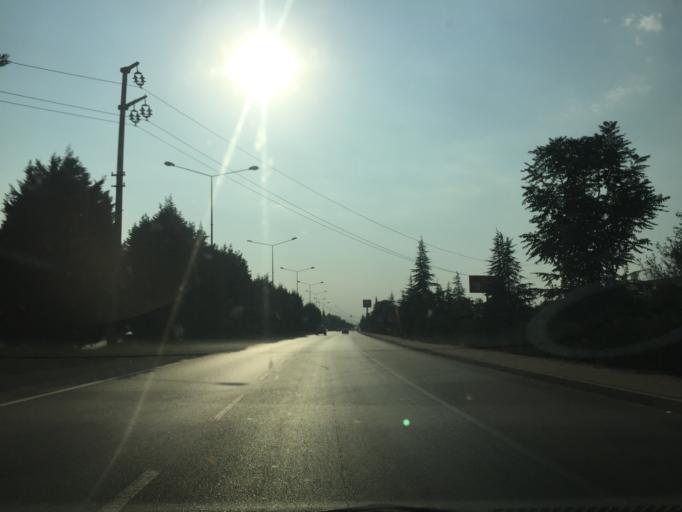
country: TR
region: Manisa
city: Salihli
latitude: 38.4894
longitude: 28.1545
